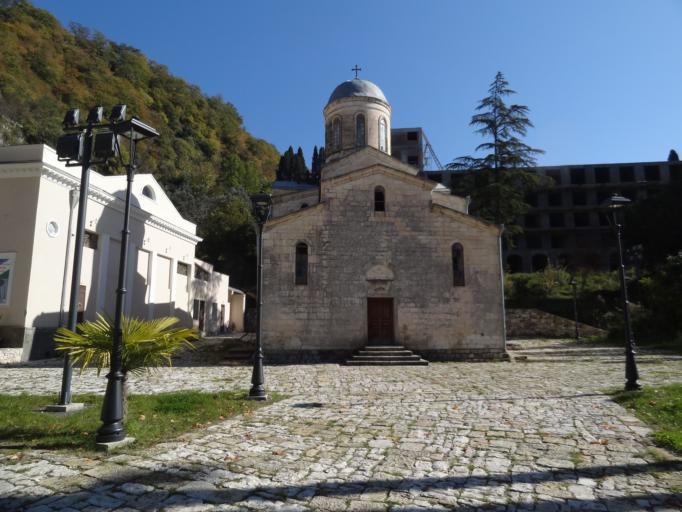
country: GE
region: Abkhazia
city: Stantsiya Novyy Afon
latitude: 43.0906
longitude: 40.8160
